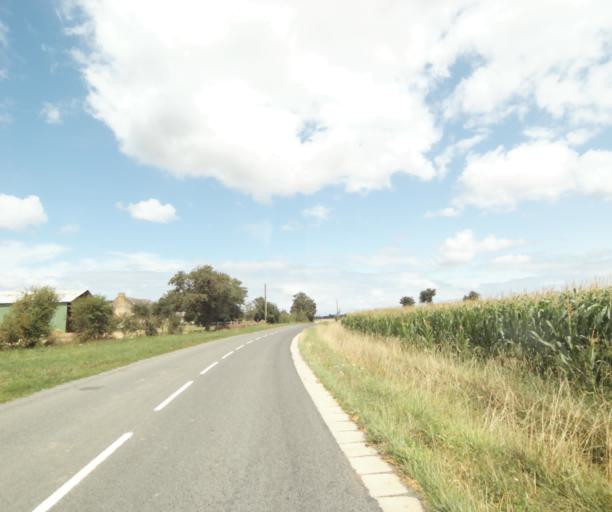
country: FR
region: Pays de la Loire
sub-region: Departement de la Sarthe
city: Sable-sur-Sarthe
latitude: 47.8521
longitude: -0.3322
